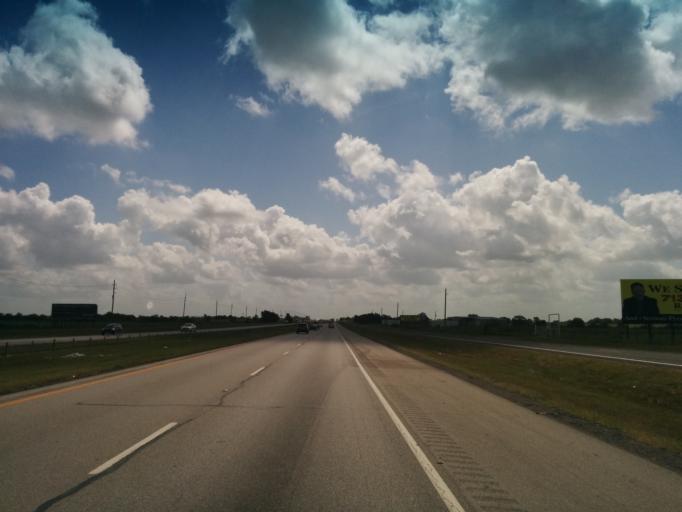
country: US
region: Texas
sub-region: Austin County
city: Sealy
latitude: 29.7552
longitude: -96.2457
